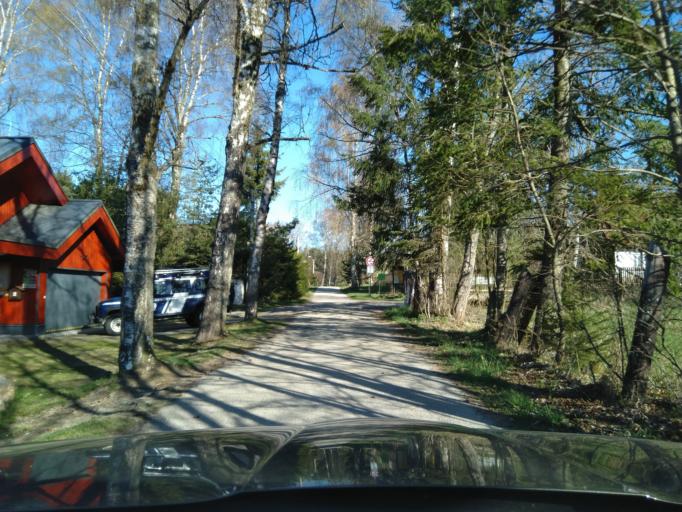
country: CZ
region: Jihocesky
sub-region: Okres Cesky Krumlov
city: Horni Plana
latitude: 48.7783
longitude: 13.9298
